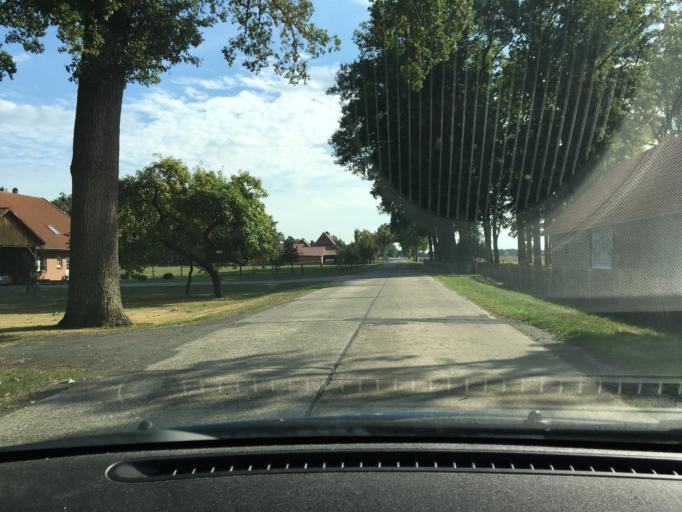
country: DE
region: Lower Saxony
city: Wietzendorf
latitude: 52.9640
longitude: 9.9724
